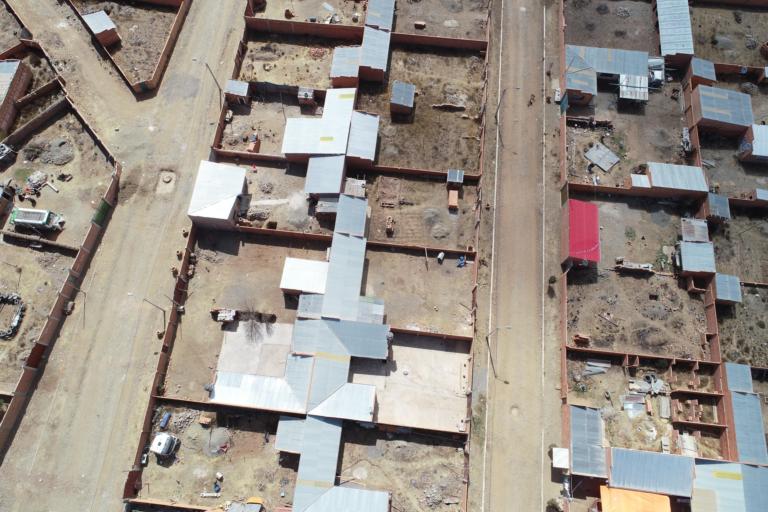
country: BO
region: La Paz
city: La Paz
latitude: -16.5962
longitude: -68.2104
